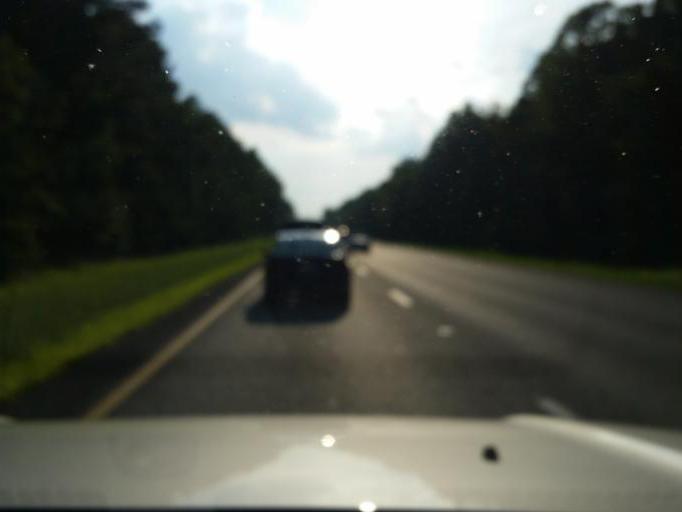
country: US
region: Virginia
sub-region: New Kent County
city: New Kent
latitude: 37.4991
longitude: -77.0486
